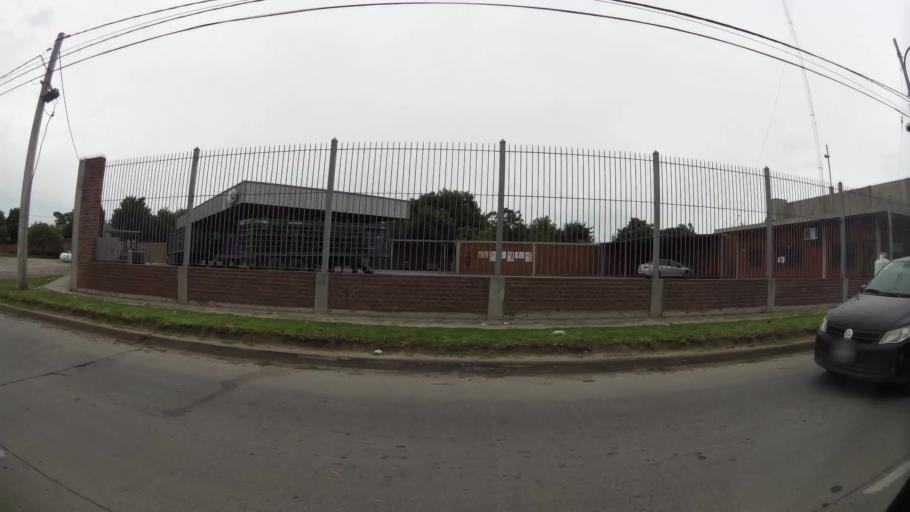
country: AR
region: Buenos Aires
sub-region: Partido de Campana
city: Campana
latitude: -34.2070
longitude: -58.9327
